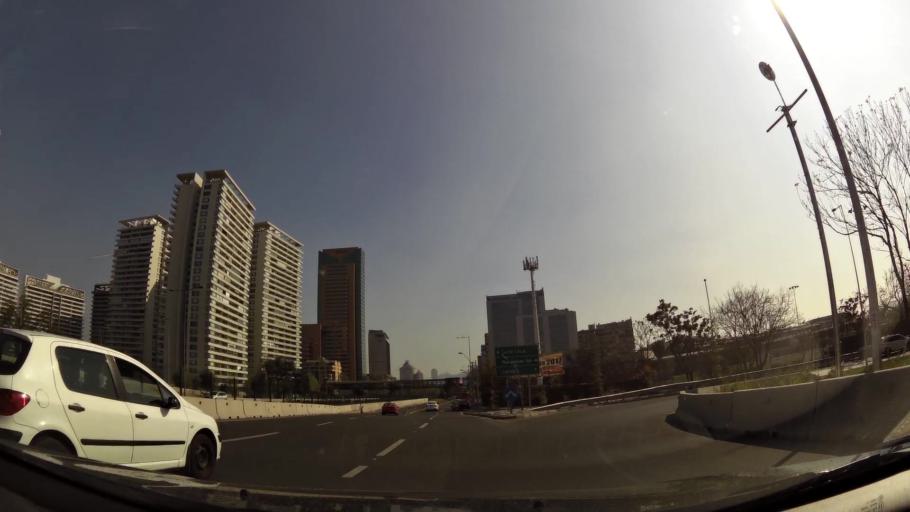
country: CL
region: Santiago Metropolitan
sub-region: Provincia de Santiago
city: Villa Presidente Frei, Nunoa, Santiago, Chile
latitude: -33.3977
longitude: -70.5715
